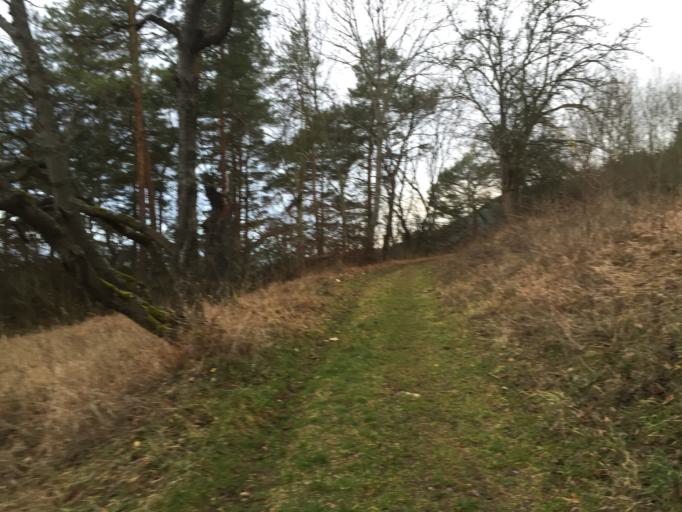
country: DE
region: Thuringia
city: Bad Blankenburg
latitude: 50.6980
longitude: 11.2555
